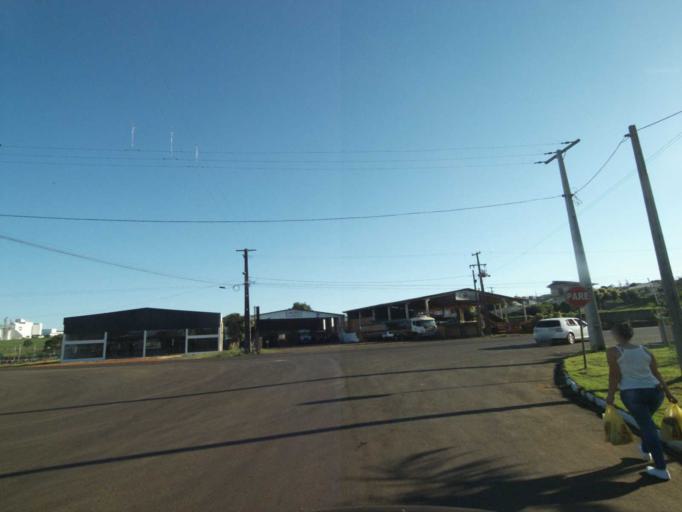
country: BR
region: Parana
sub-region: Coronel Vivida
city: Coronel Vivida
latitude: -25.9784
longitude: -52.8150
